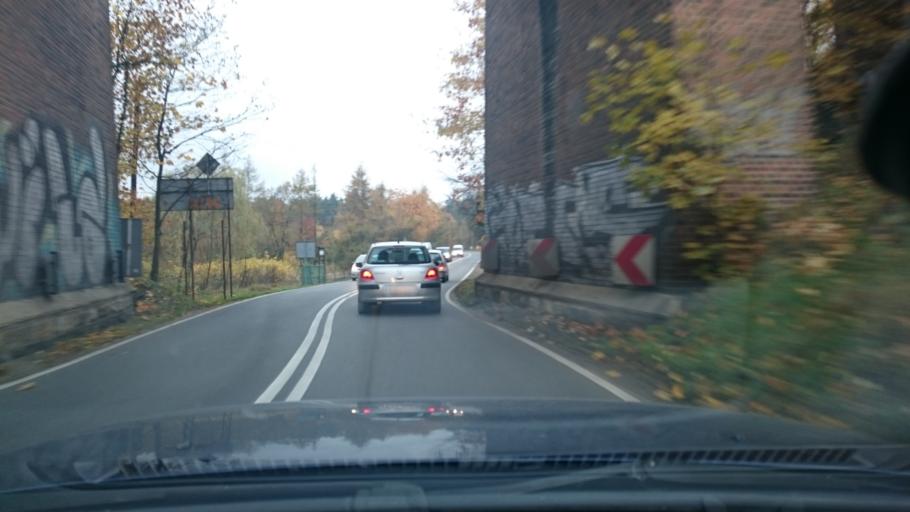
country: PL
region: Silesian Voivodeship
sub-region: Rybnik
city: Rybnik
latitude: 50.1058
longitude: 18.5717
